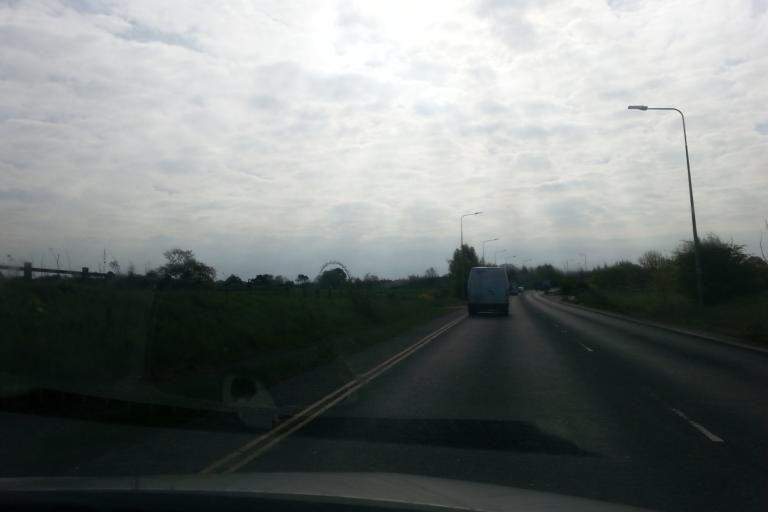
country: GB
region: England
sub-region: Suffolk
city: Bramford
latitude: 52.0482
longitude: 1.1035
